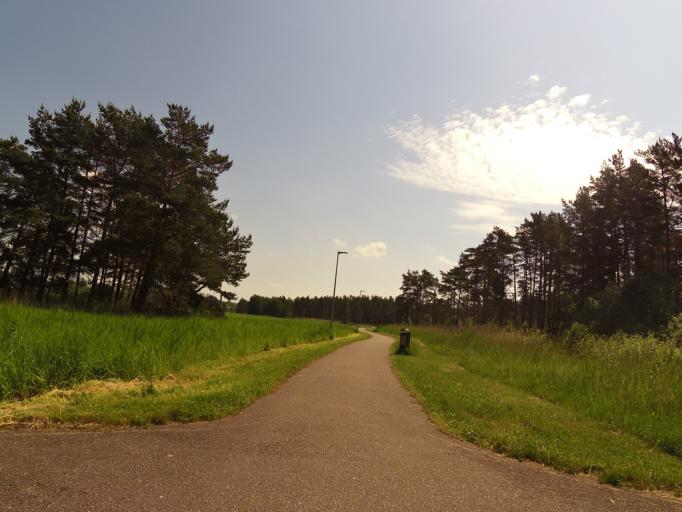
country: EE
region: Laeaene
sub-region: Haapsalu linn
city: Haapsalu
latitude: 58.9401
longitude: 23.5196
